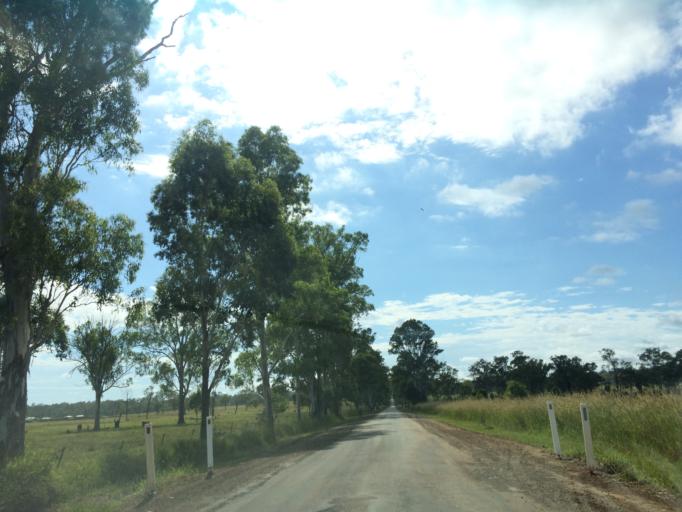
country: AU
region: Queensland
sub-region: Logan
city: Cedar Vale
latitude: -27.8798
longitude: 152.9572
